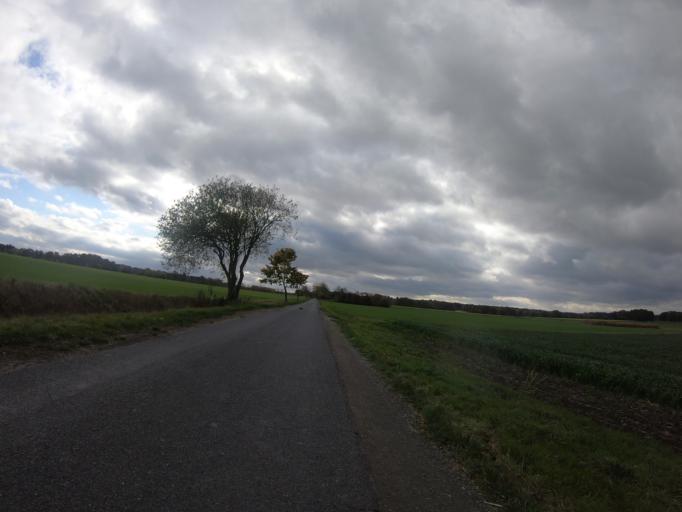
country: DE
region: Lower Saxony
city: Ribbesbuttel
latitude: 52.4221
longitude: 10.4833
